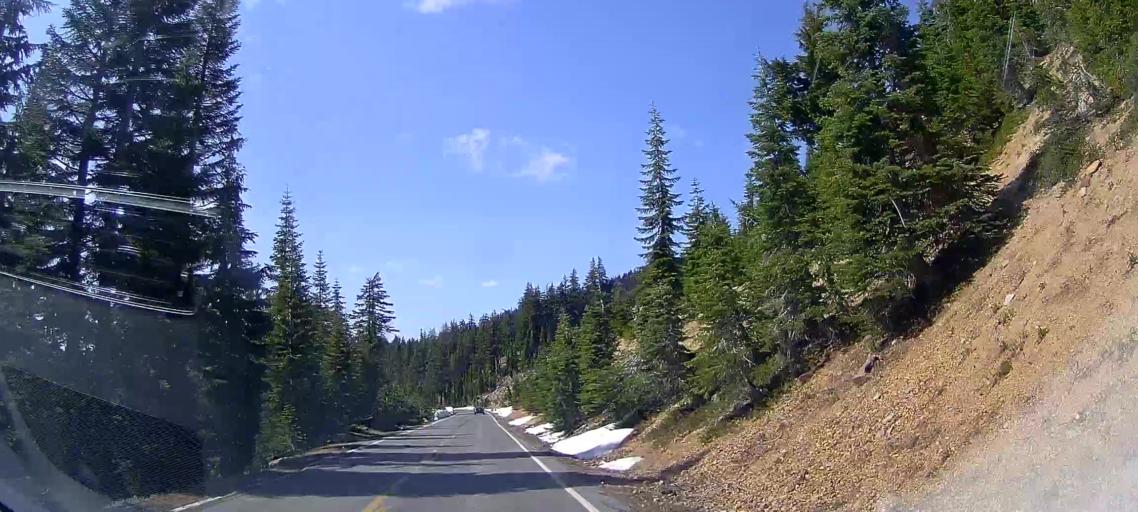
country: US
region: Oregon
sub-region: Klamath County
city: Klamath Falls
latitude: 42.8983
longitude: -122.0993
